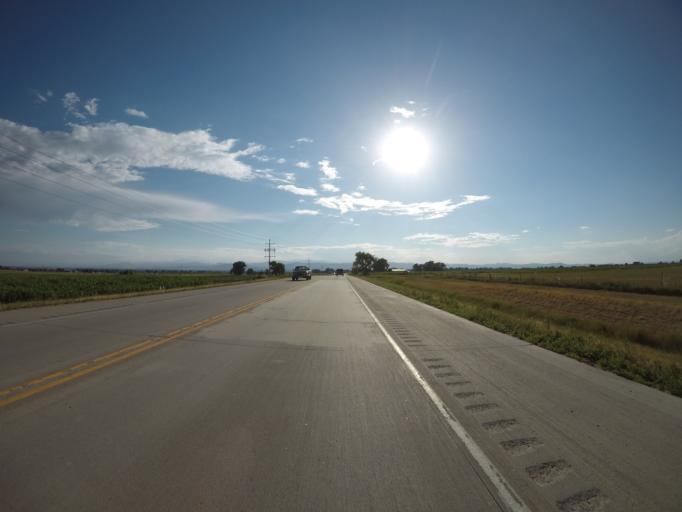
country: US
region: Colorado
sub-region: Weld County
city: Severance
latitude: 40.5812
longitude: -104.9345
